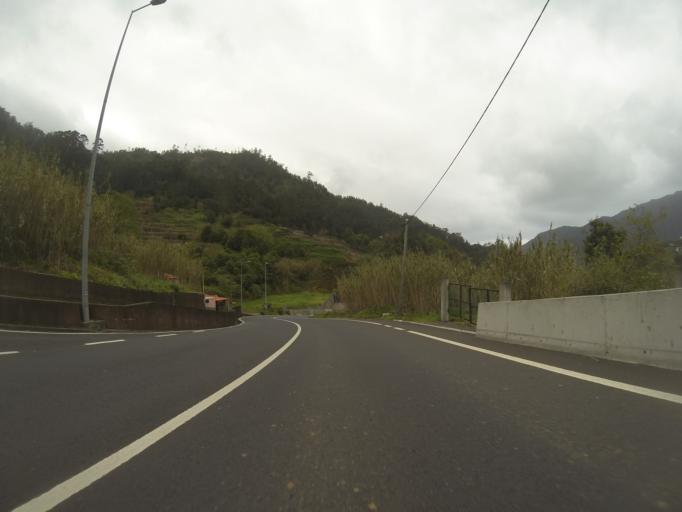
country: PT
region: Madeira
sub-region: Sao Vicente
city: Sao Vicente
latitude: 32.7765
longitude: -17.0324
